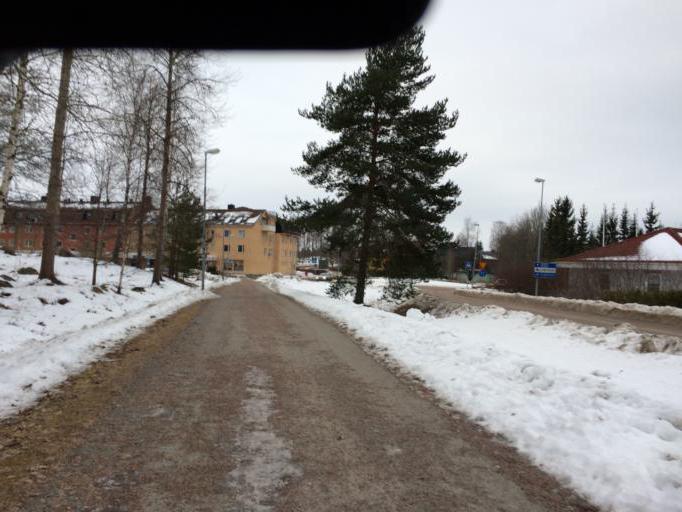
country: SE
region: Vaestmanland
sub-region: Hallstahammars Kommun
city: Hallstahammar
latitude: 59.6176
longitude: 16.2249
